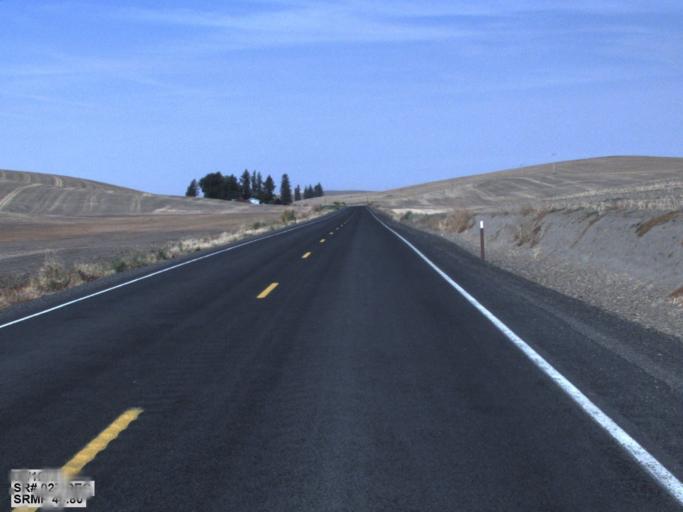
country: US
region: Idaho
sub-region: Benewah County
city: Plummer
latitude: 47.1946
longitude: -117.1202
